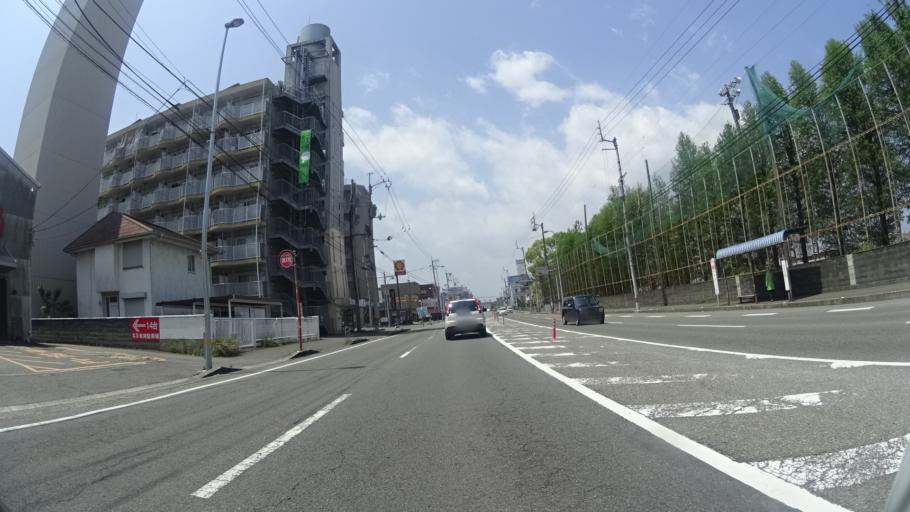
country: JP
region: Tokushima
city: Tokushima-shi
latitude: 34.0723
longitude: 134.5070
